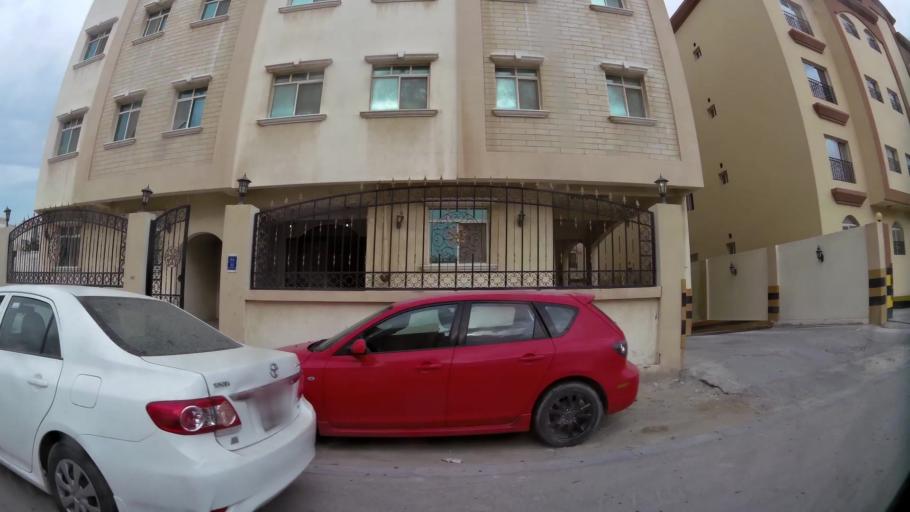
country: QA
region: Baladiyat ad Dawhah
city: Doha
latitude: 25.2762
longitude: 51.4957
